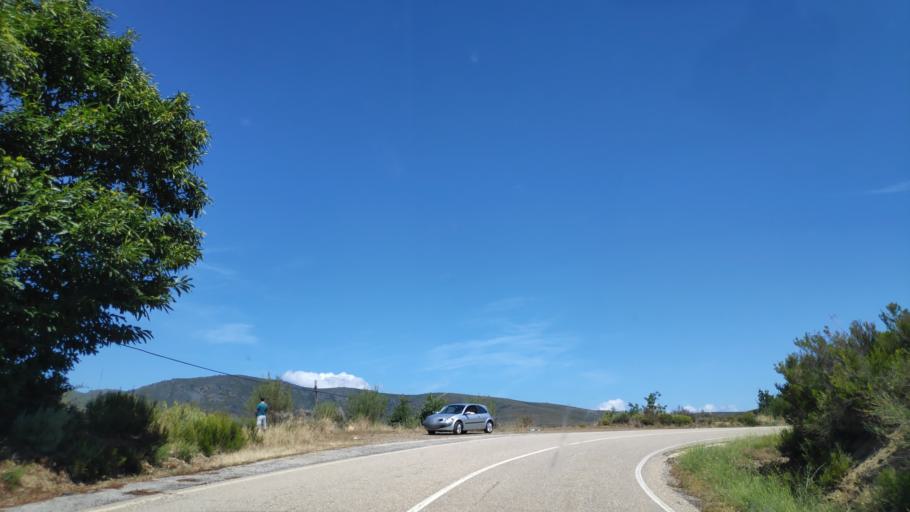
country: ES
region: Castille and Leon
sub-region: Provincia de Zamora
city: Requejo
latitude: 41.9723
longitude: -6.7143
